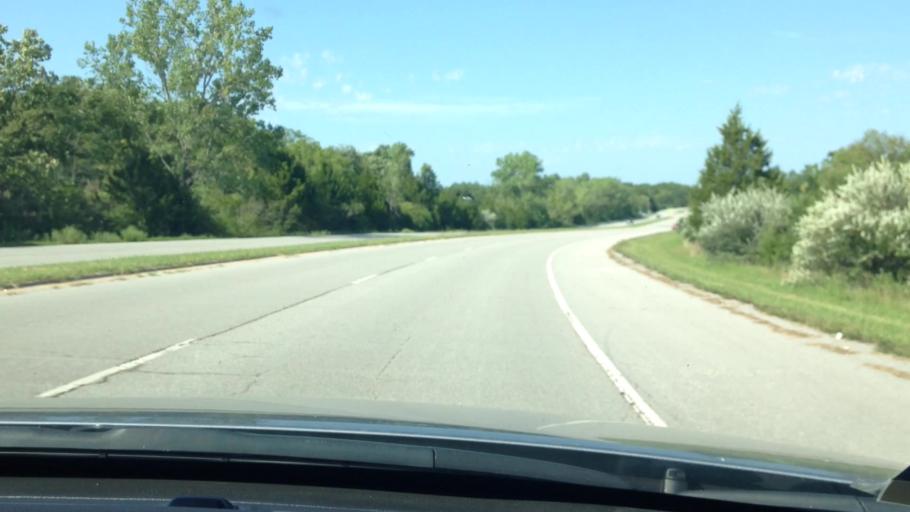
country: US
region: Missouri
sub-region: Jackson County
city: Grandview
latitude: 38.8949
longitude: -94.4937
